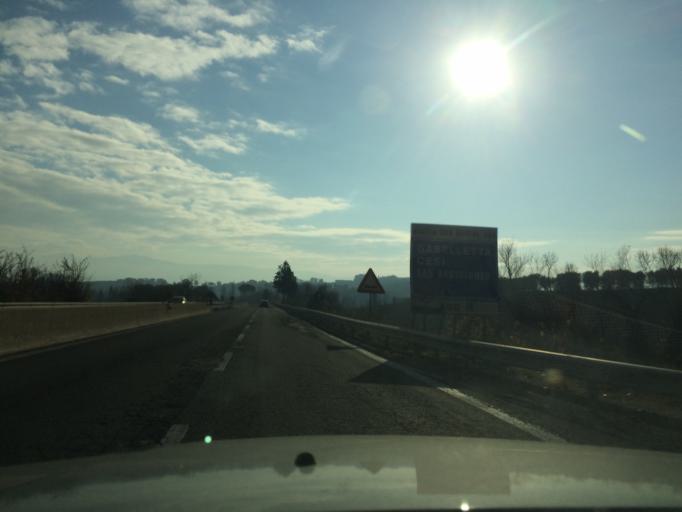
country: IT
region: Umbria
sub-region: Provincia di Terni
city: San Gemini
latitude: 42.5976
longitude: 12.5632
